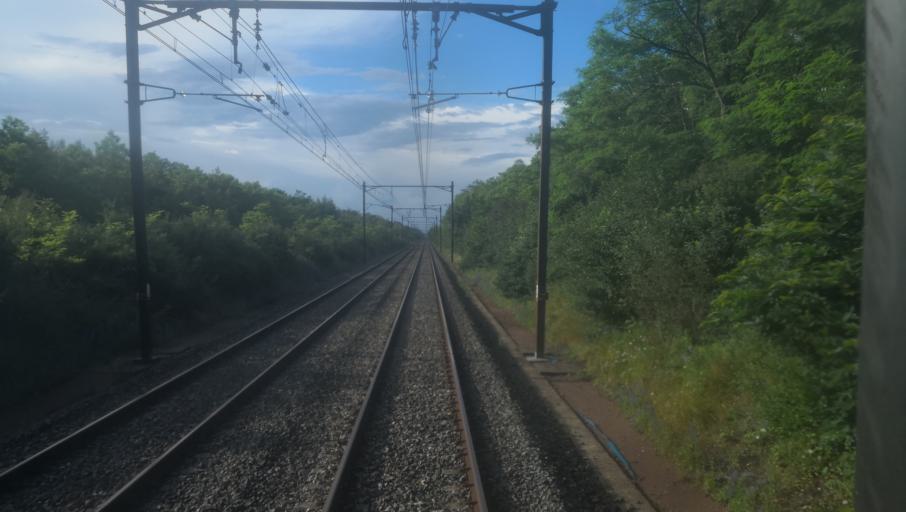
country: FR
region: Centre
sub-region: Departement du Loir-et-Cher
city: Salbris
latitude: 47.4772
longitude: 2.0394
